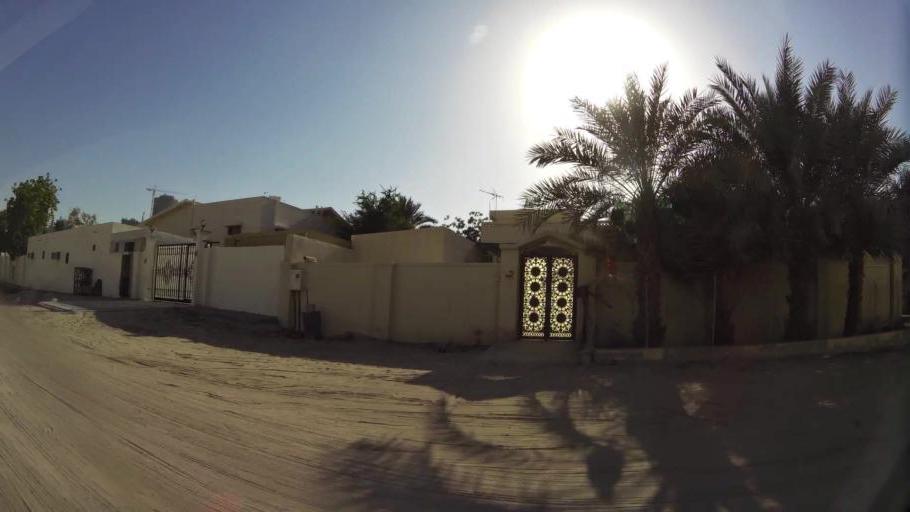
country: AE
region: Ajman
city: Ajman
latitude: 25.4014
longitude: 55.4587
